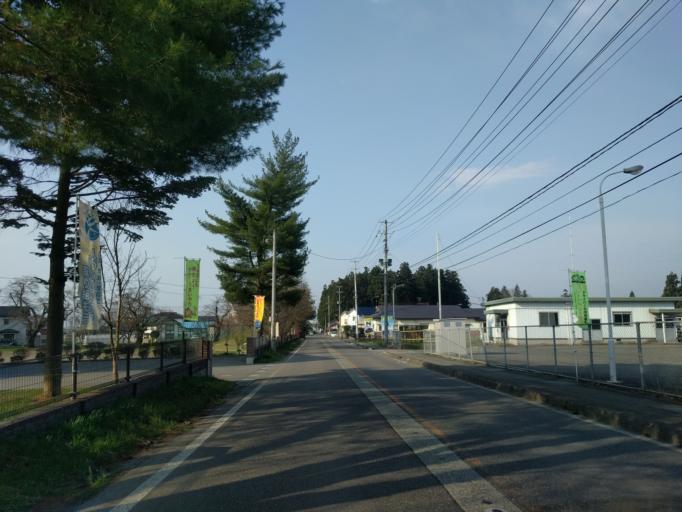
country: JP
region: Fukushima
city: Kitakata
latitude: 37.6682
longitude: 139.8870
